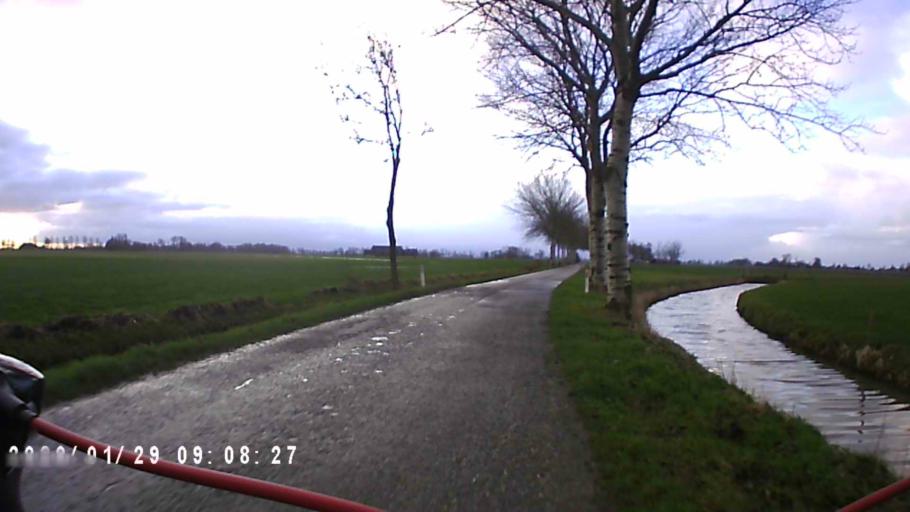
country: NL
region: Groningen
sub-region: Gemeente Zuidhorn
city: Aduard
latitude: 53.3152
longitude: 6.4552
